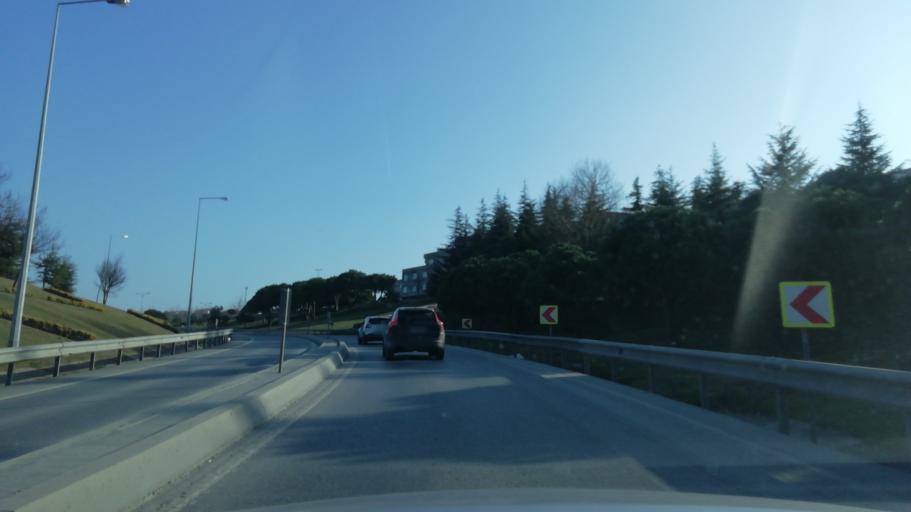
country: TR
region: Istanbul
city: Esenyurt
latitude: 41.0469
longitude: 28.6889
